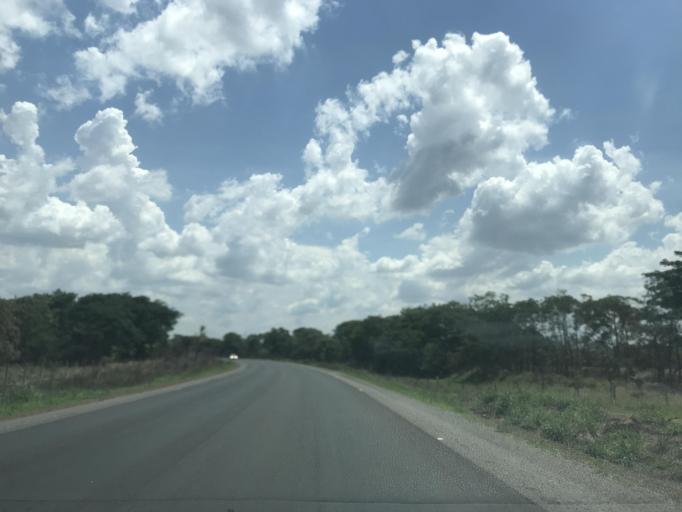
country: BR
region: Goias
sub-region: Piracanjuba
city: Piracanjuba
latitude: -17.3022
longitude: -48.7980
